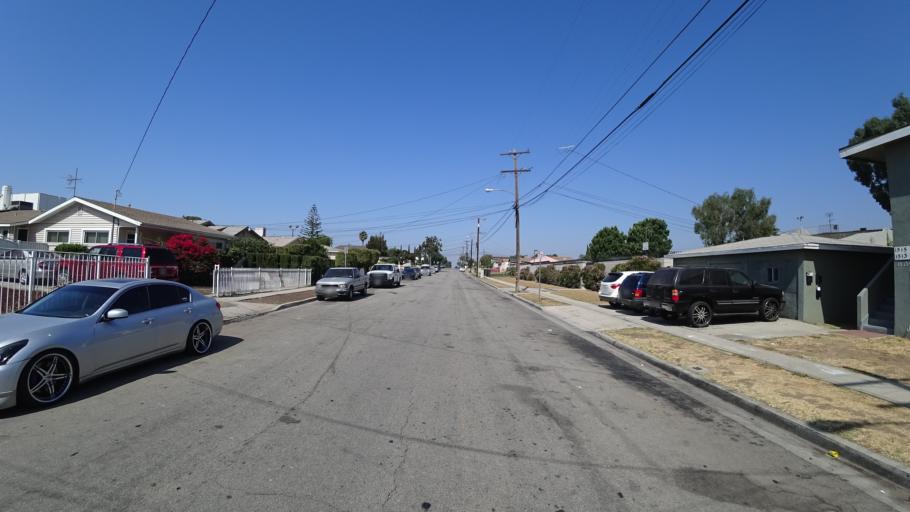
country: US
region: California
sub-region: Los Angeles County
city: Westmont
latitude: 33.9391
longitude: -118.3029
